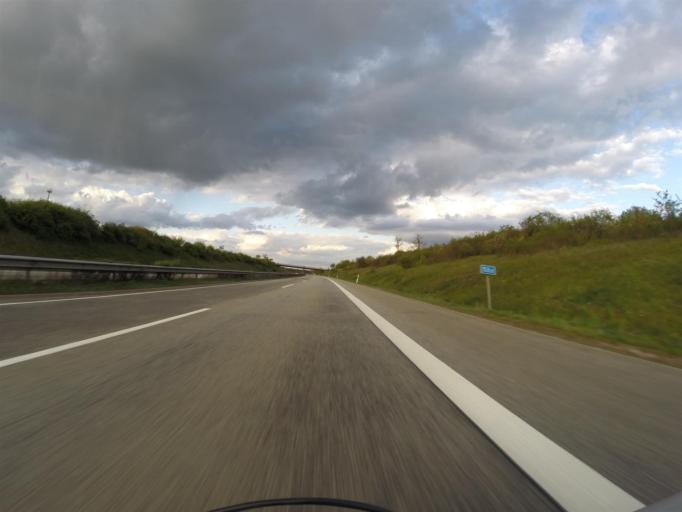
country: DE
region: Rheinland-Pfalz
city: Borrstadt
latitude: 49.5829
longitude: 7.9356
